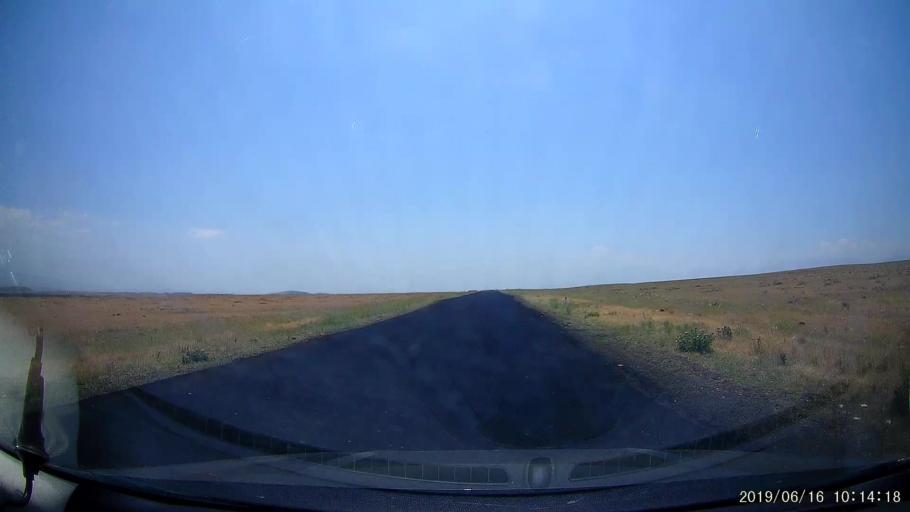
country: TR
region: Igdir
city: Tuzluca
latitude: 40.1860
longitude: 43.6600
